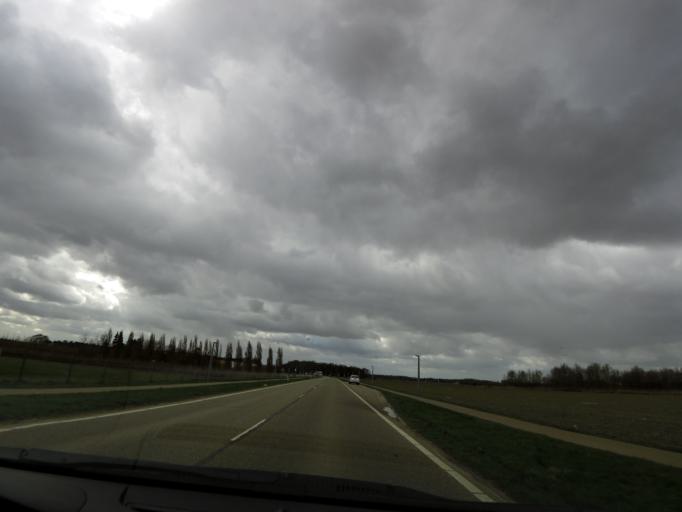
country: NL
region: Limburg
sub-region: Gemeente Beesel
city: Reuver
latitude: 51.2734
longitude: 6.0728
